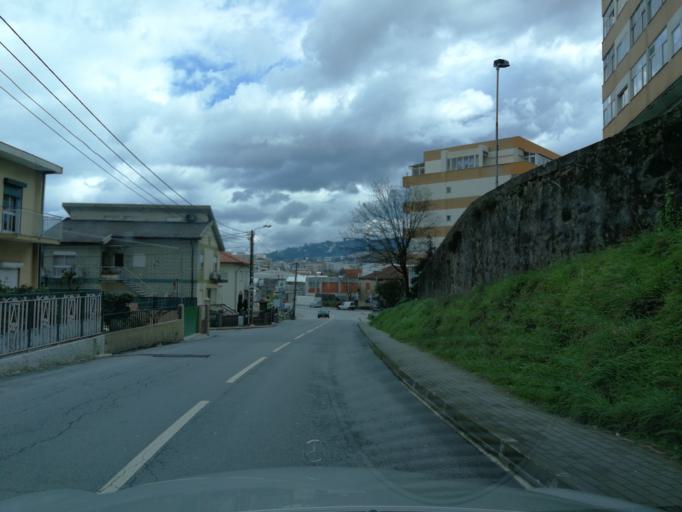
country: PT
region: Braga
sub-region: Braga
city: Braga
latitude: 41.5408
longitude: -8.4269
